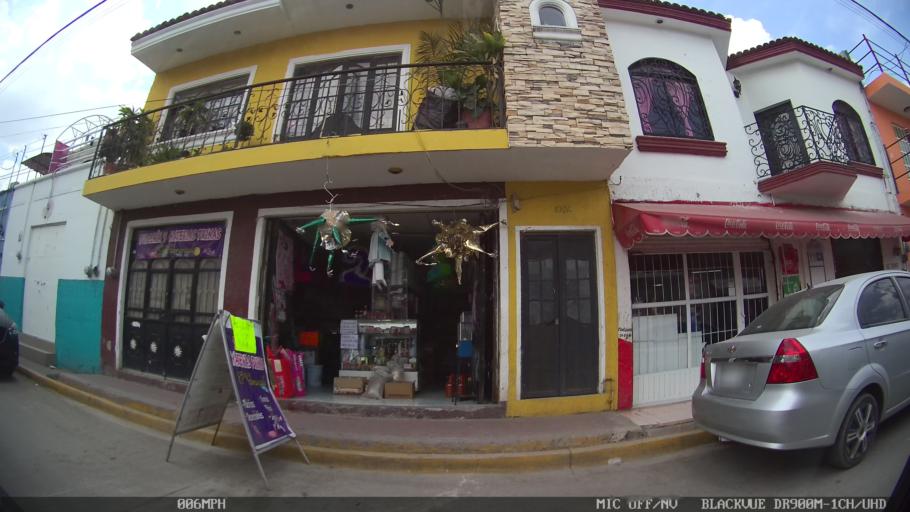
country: MX
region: Jalisco
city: Tonala
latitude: 20.6758
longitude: -103.2429
